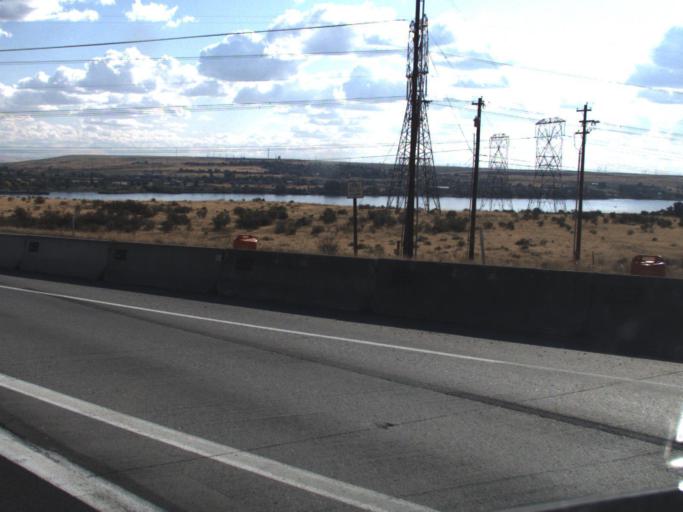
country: US
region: Oregon
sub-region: Umatilla County
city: Umatilla
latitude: 45.9423
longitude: -119.3338
